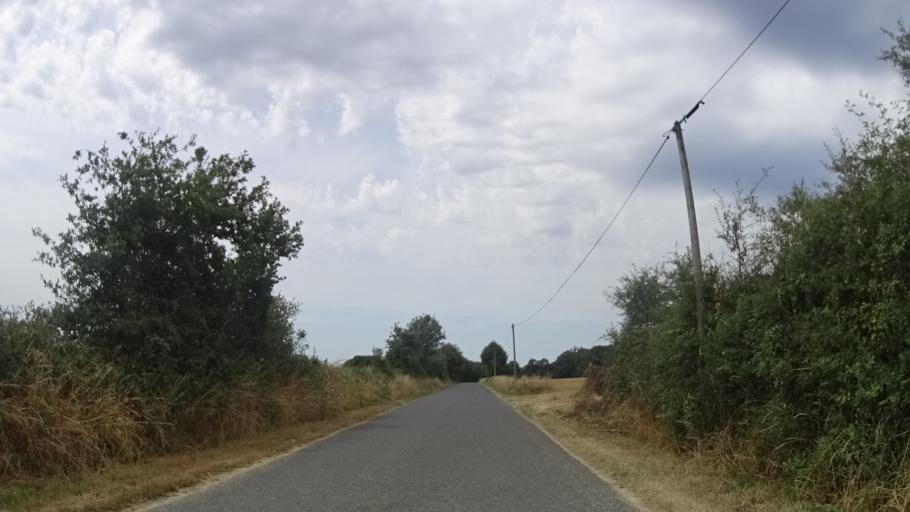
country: FR
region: Pays de la Loire
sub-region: Departement de la Loire-Atlantique
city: Fay-de-Bretagne
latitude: 47.4229
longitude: -1.7617
